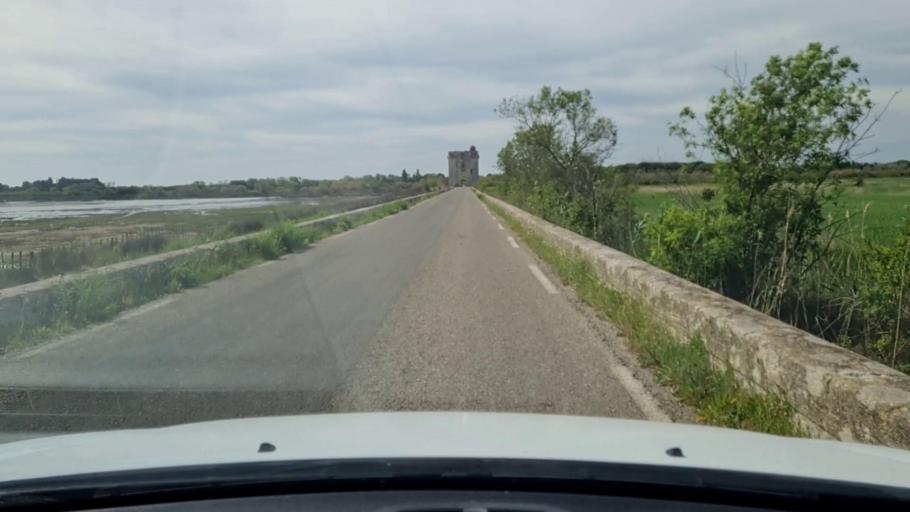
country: FR
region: Languedoc-Roussillon
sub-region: Departement du Gard
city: Aigues-Mortes
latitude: 43.5948
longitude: 4.2084
